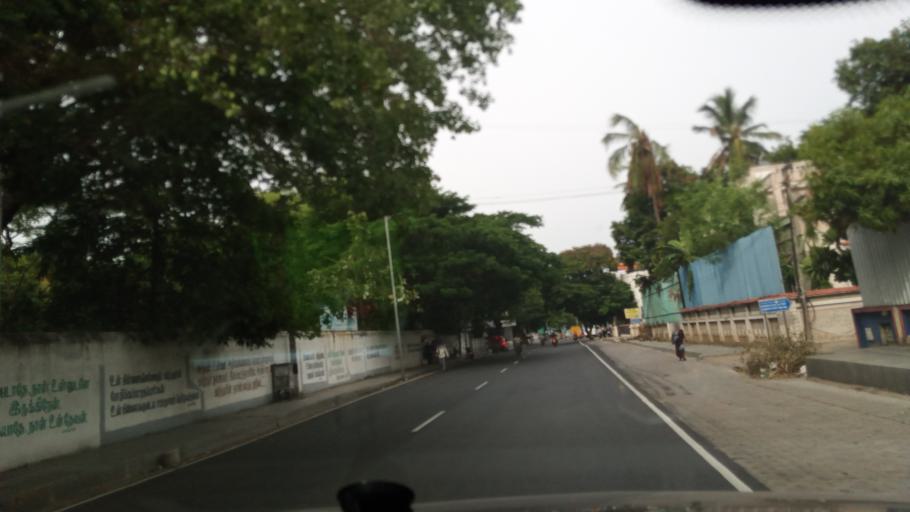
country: IN
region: Tamil Nadu
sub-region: Kancheepuram
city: Saint Thomas Mount
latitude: 13.0086
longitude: 80.1999
